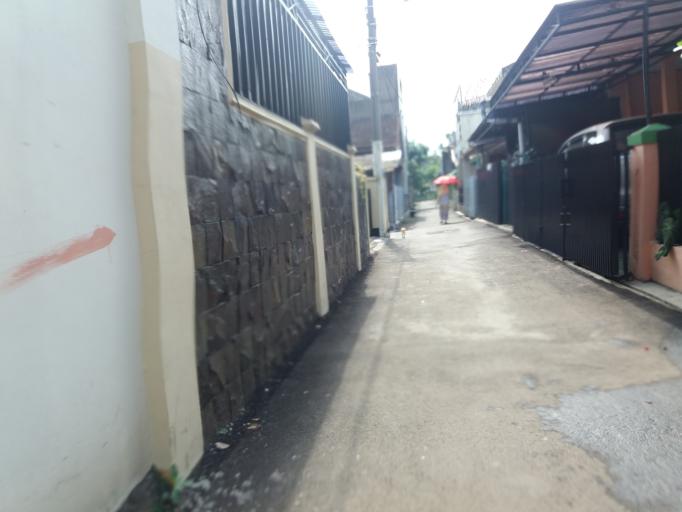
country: ID
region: West Java
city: Bandung
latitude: -6.9176
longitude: 107.6627
